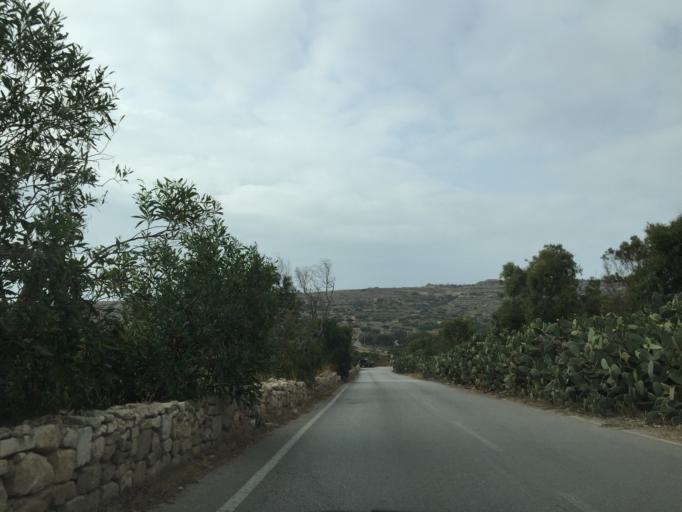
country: MT
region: Il-Mellieha
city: Mellieha
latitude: 35.9433
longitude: 14.3526
